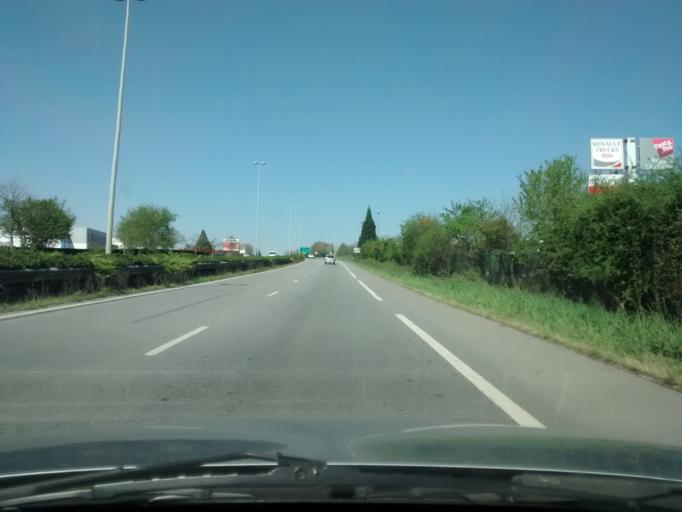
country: FR
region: Pays de la Loire
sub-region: Departement de la Mayenne
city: Laval
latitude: 48.0891
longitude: -0.7409
